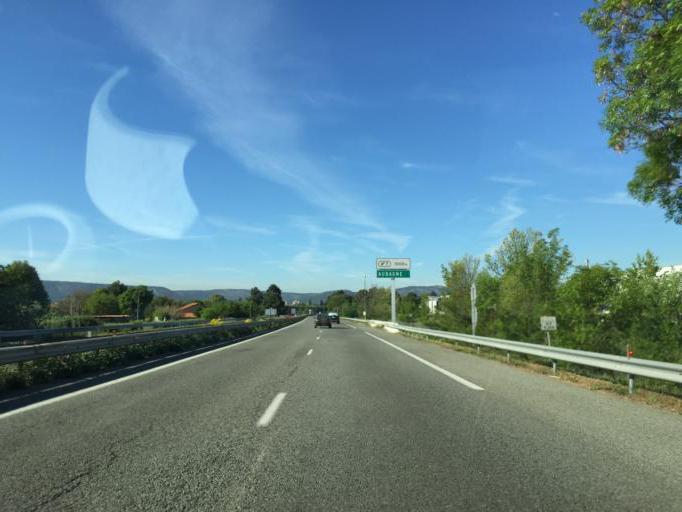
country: FR
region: Provence-Alpes-Cote d'Azur
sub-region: Departement des Bouches-du-Rhone
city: Aubagne
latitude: 43.3142
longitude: 5.5847
